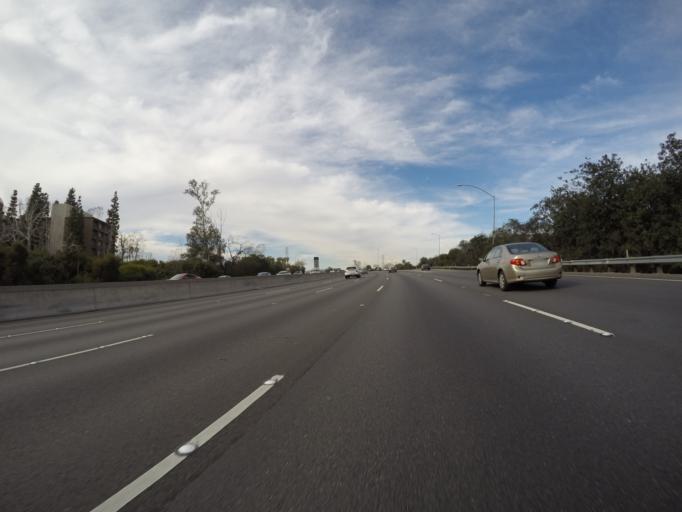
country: US
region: California
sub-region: Los Angeles County
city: Universal City
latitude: 34.1453
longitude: -118.3680
